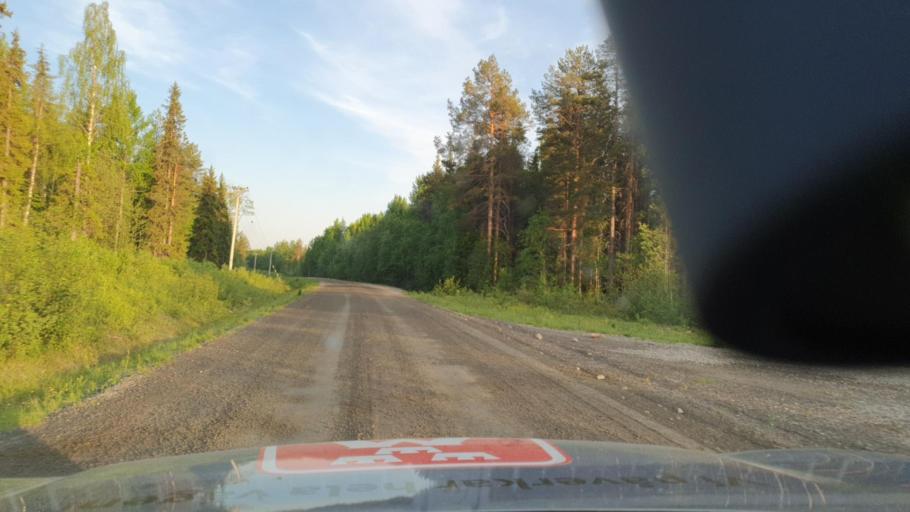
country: SE
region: Norrbotten
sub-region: Bodens Kommun
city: Boden
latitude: 66.1844
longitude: 21.5027
